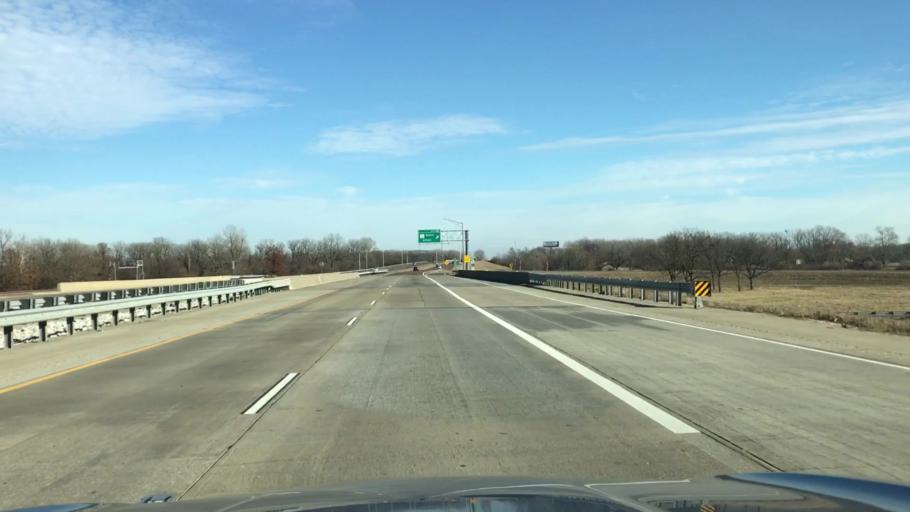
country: US
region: Illinois
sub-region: Madison County
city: Mitchell
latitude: 38.7660
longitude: -90.1252
